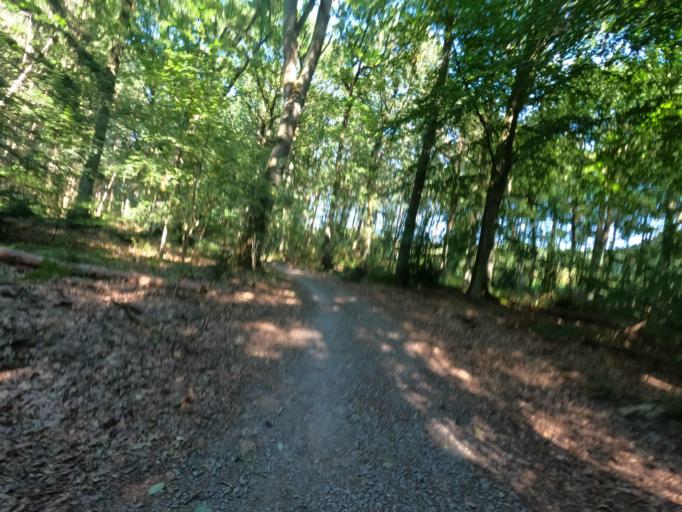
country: DE
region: North Rhine-Westphalia
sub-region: Regierungsbezirk Koln
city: Wassenberg
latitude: 51.1568
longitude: 6.1743
